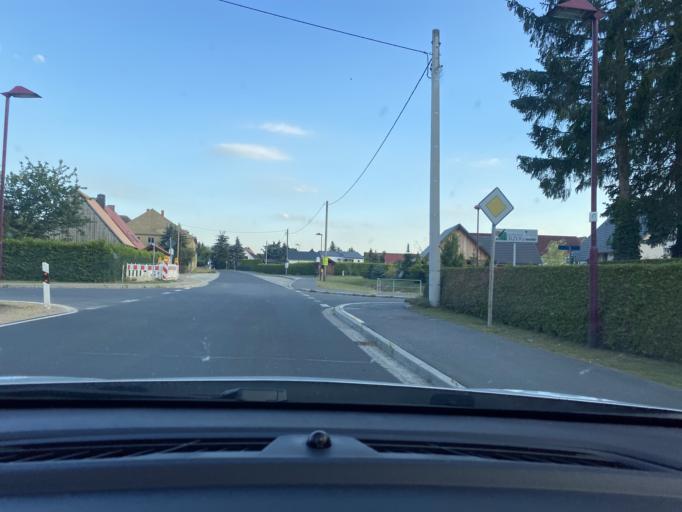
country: DE
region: Saxony
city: Kodersdorf
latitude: 51.2637
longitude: 14.8851
